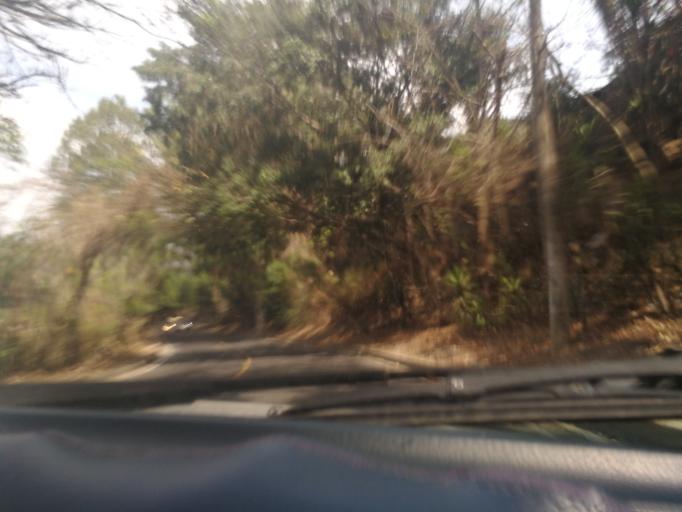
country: GT
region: Guatemala
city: Guatemala City
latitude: 14.6236
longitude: -90.4813
